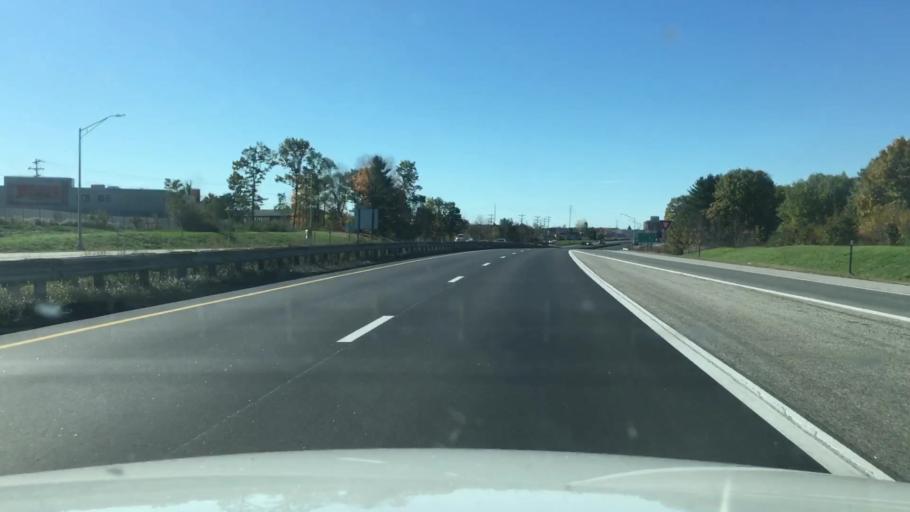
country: US
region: Maine
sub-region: Cumberland County
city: South Portland Gardens
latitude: 43.6454
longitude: -70.3323
